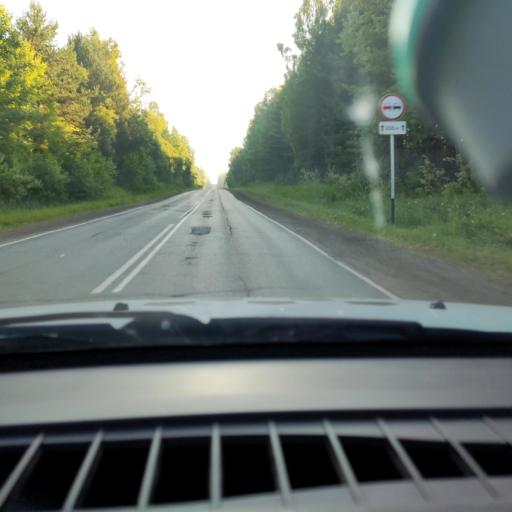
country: RU
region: Perm
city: Kungur
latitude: 57.3517
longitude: 56.8010
